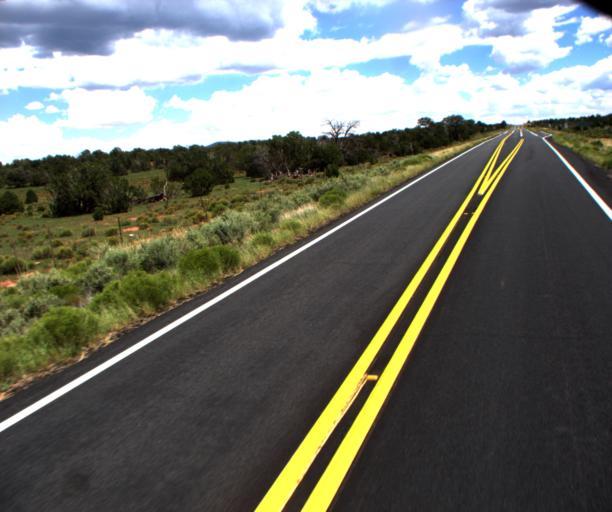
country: US
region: Arizona
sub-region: Coconino County
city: Parks
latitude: 35.6052
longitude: -112.0433
